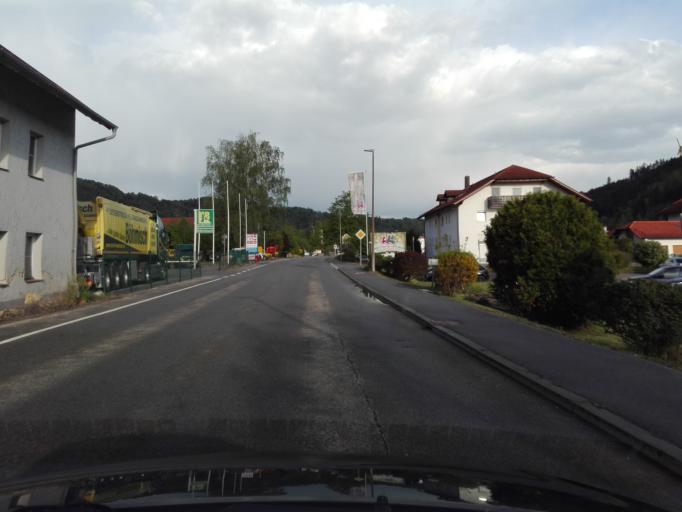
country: DE
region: Bavaria
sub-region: Lower Bavaria
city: Obernzell
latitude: 48.5565
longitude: 13.6287
